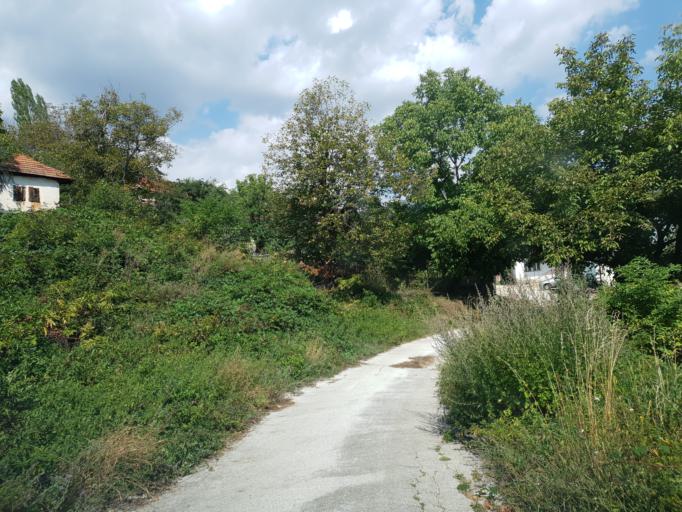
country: MK
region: Makedonski Brod
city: Samokov
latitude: 41.7458
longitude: 21.1045
